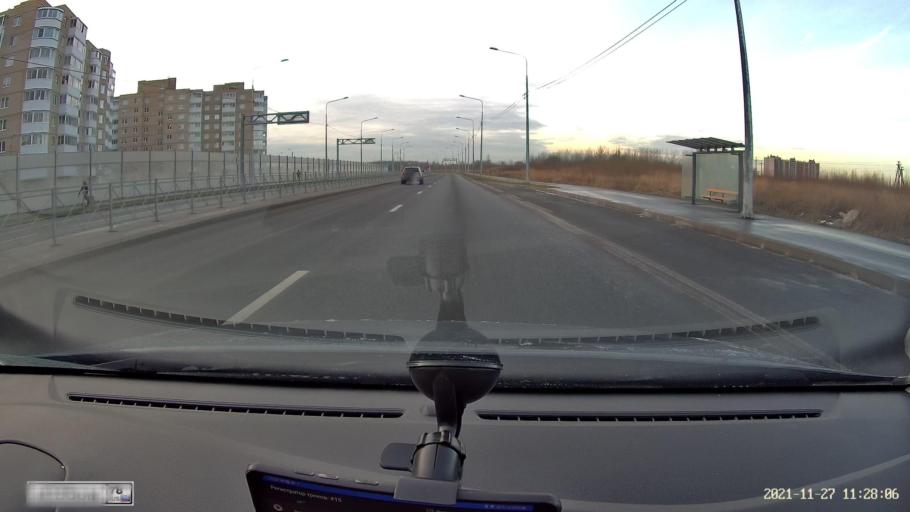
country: RU
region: St.-Petersburg
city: Krasnoye Selo
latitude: 59.7468
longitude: 30.0782
